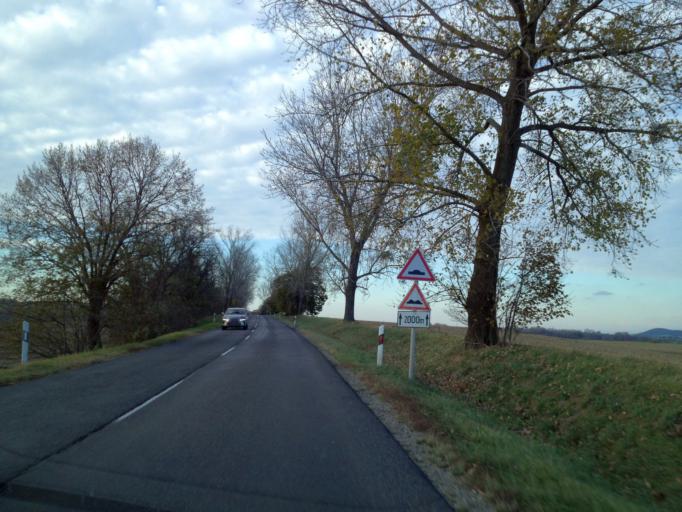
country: HU
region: Gyor-Moson-Sopron
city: Bakonyszentlaszlo
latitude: 47.4541
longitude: 17.8094
